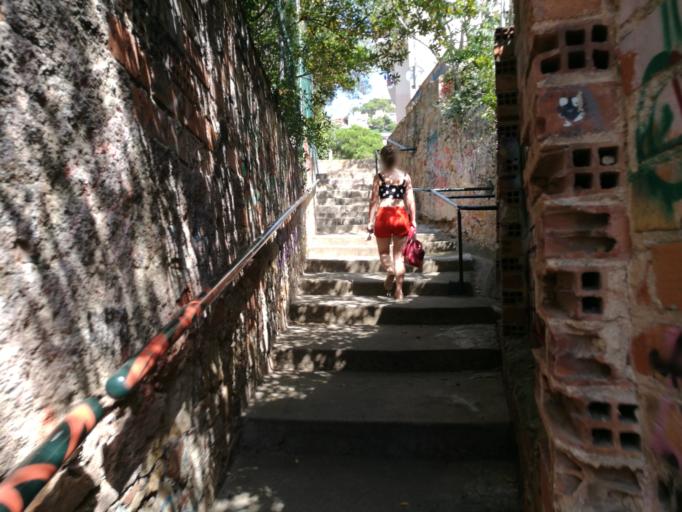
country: ES
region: Catalonia
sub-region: Provincia de Girona
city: Blanes
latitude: 41.6759
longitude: 2.7943
